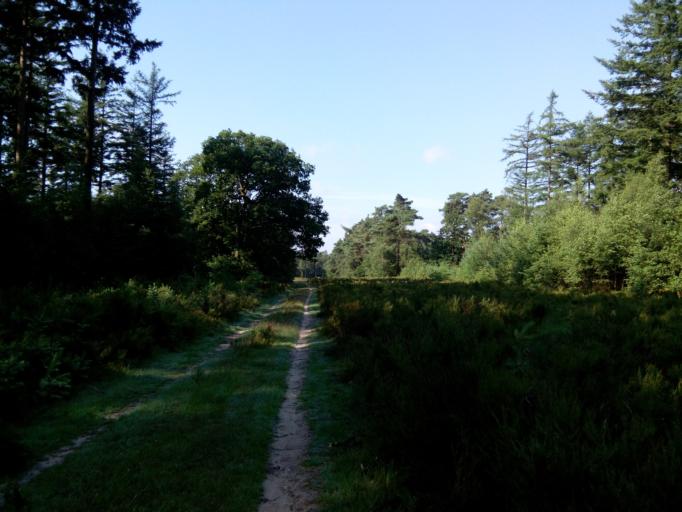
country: NL
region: Utrecht
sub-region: Gemeente Utrechtse Heuvelrug
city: Maarn
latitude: 52.0760
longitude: 5.3456
